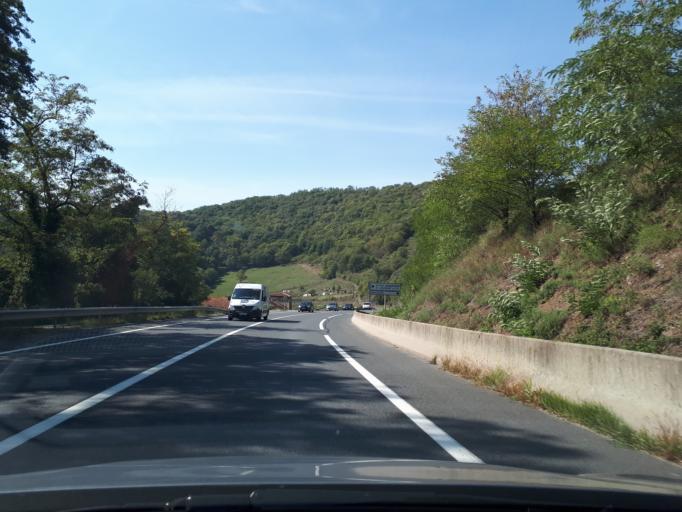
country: FR
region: Rhone-Alpes
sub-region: Departement du Rhone
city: Saint-Laurent-de-Chamousset
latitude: 45.7395
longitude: 4.5146
